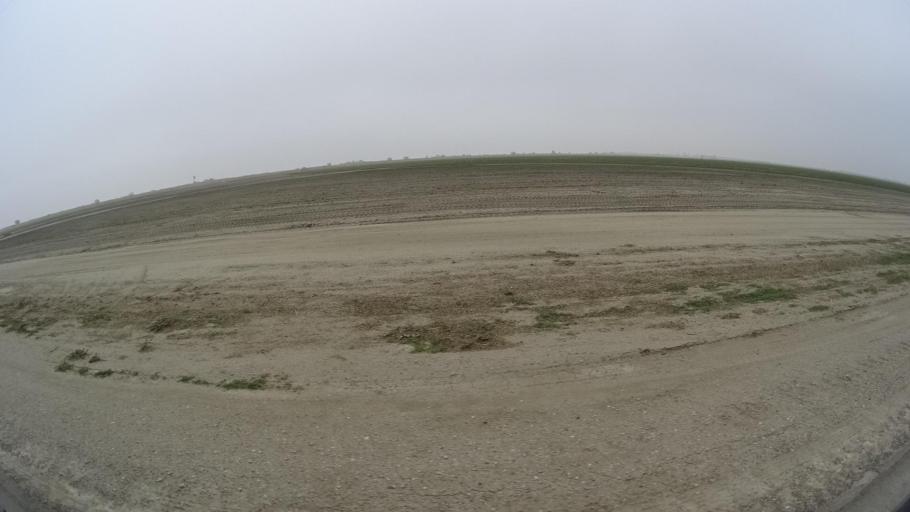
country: US
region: California
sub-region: Kern County
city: Rosedale
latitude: 35.2178
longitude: -119.2329
